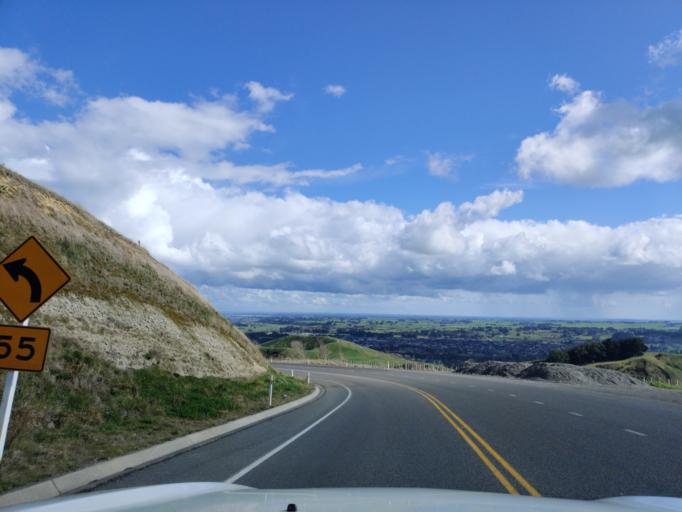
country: NZ
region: Manawatu-Wanganui
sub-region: Palmerston North City
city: Palmerston North
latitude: -40.2860
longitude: 175.7882
